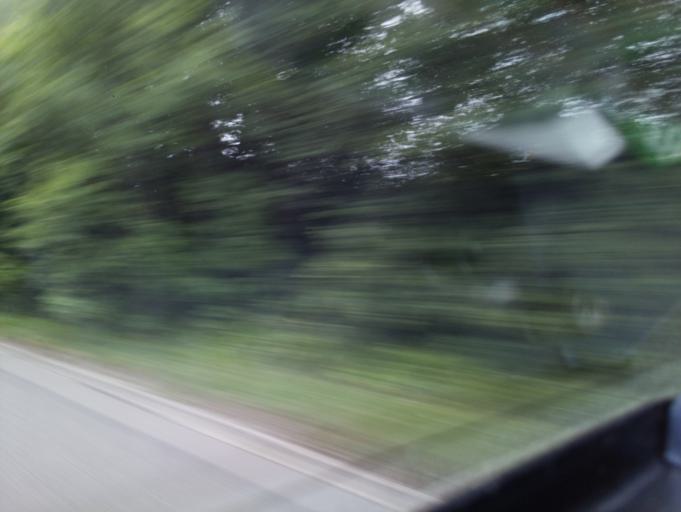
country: GB
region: England
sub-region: Worcestershire
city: Droitwich
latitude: 52.2702
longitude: -2.1665
